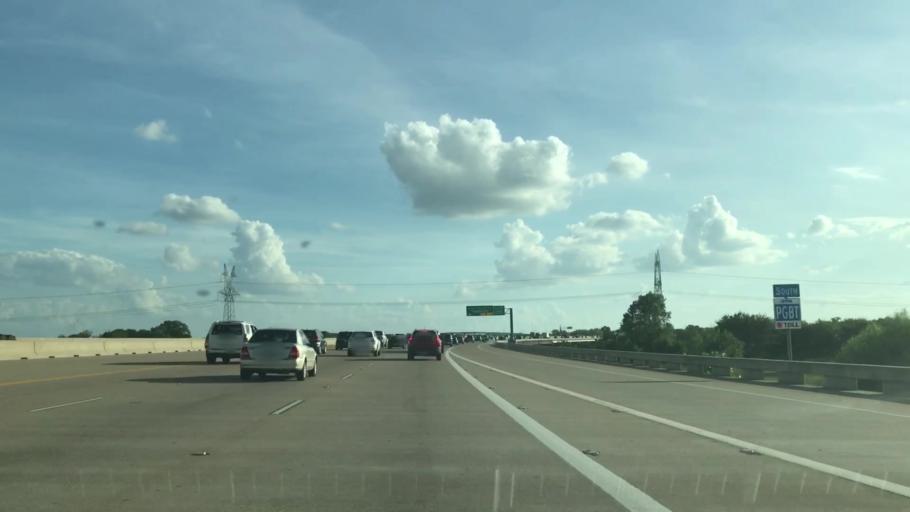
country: US
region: Texas
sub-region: Dallas County
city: Grand Prairie
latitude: 32.7888
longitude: -97.0192
